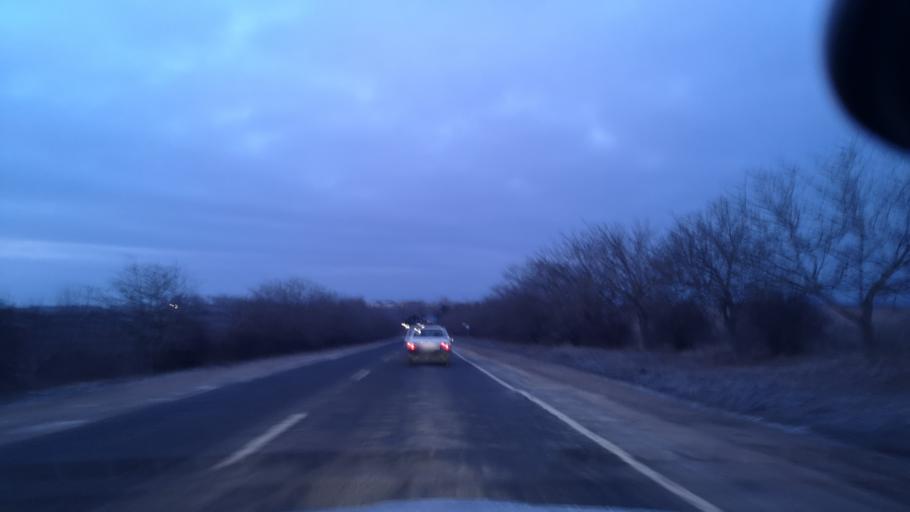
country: MD
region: Rezina
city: Rezina
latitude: 47.7449
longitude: 28.9066
